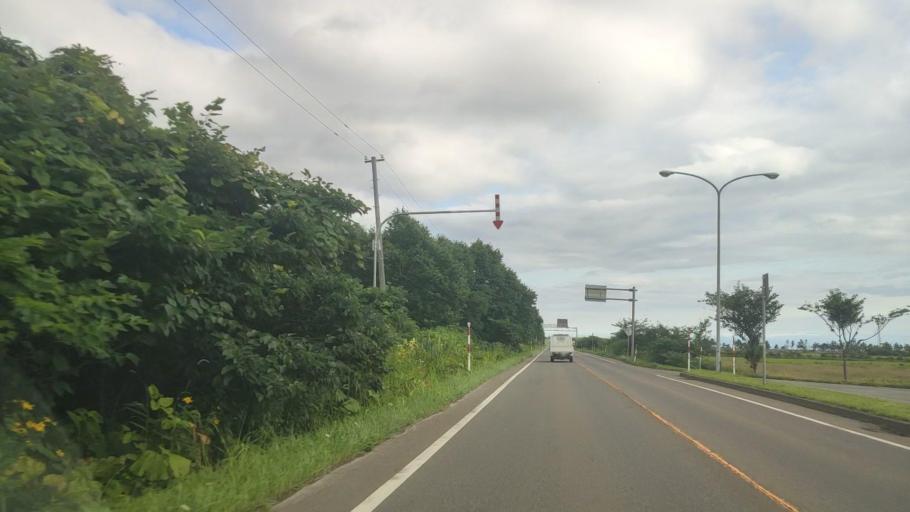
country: JP
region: Hokkaido
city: Niseko Town
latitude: 42.5858
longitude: 140.4502
